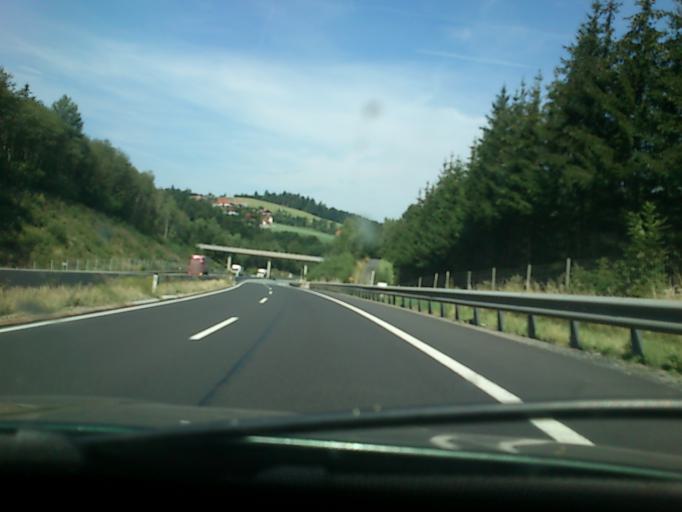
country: AT
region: Lower Austria
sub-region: Politischer Bezirk Neunkirchen
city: Zobern
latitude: 47.5074
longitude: 16.1096
